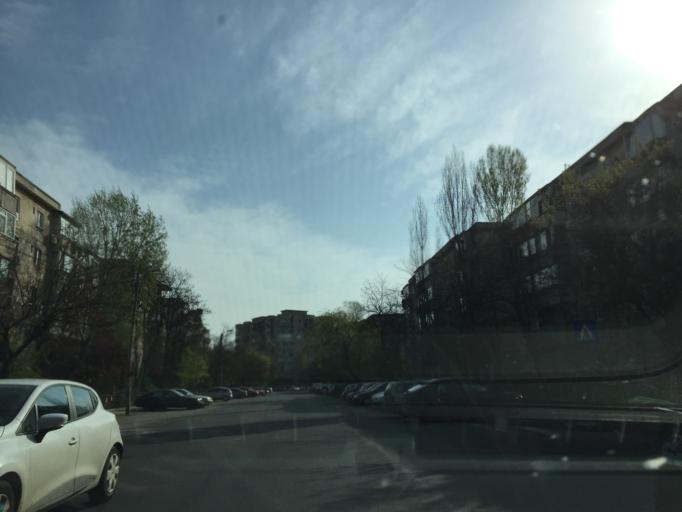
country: RO
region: Bucuresti
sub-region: Municipiul Bucuresti
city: Bucharest
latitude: 44.4167
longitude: 26.1258
